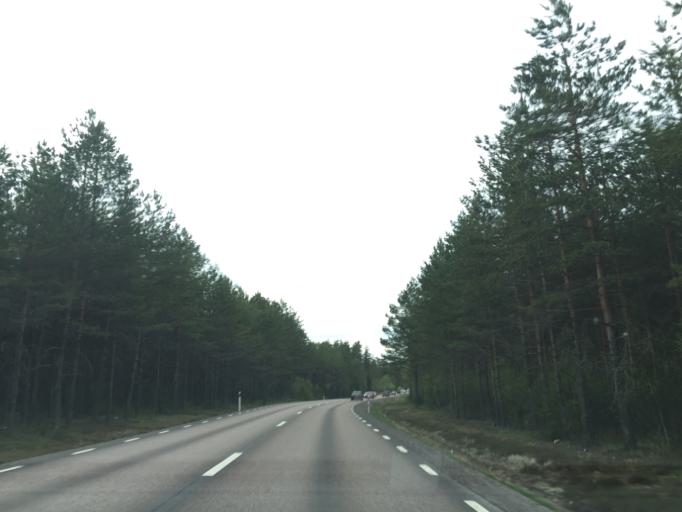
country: SE
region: Vaermland
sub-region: Eda Kommun
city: Charlottenberg
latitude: 59.9059
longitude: 12.2764
